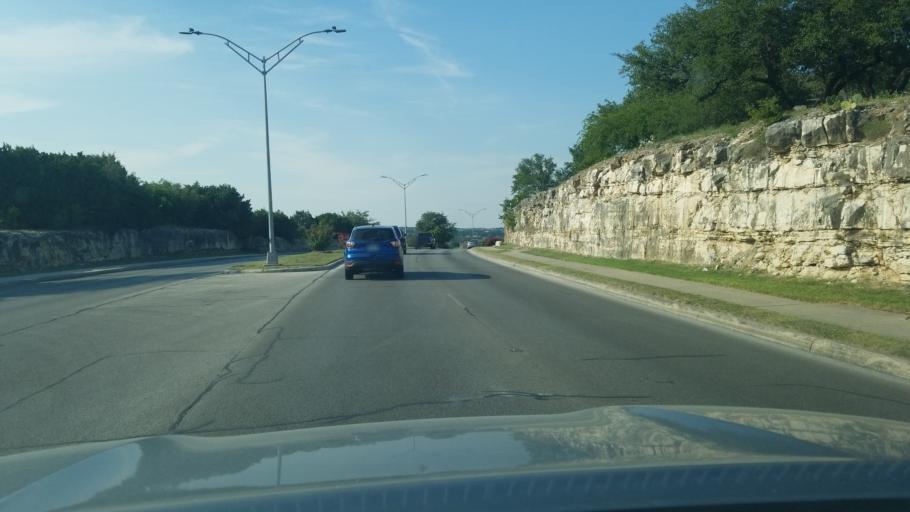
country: US
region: Texas
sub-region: Bexar County
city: Hollywood Park
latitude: 29.6412
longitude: -98.5068
